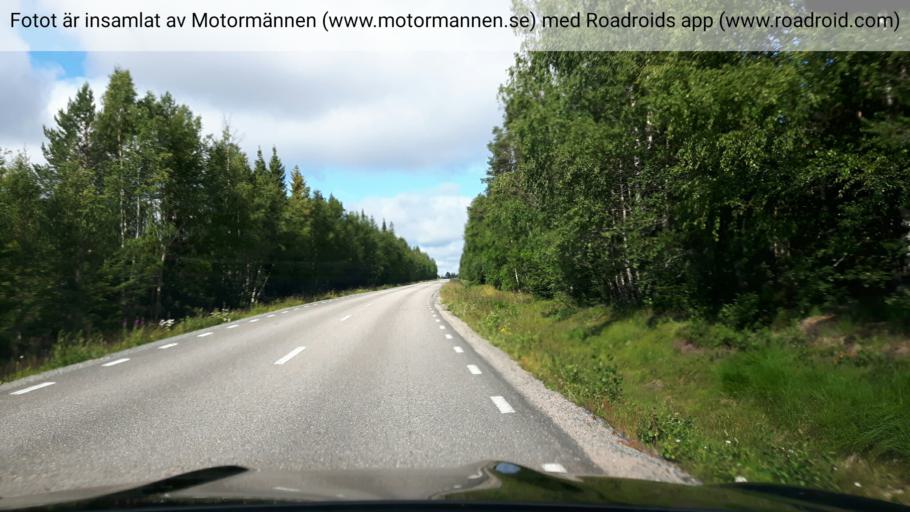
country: SE
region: Gaevleborg
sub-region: Ljusdals Kommun
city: Farila
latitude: 61.7570
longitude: 15.4164
